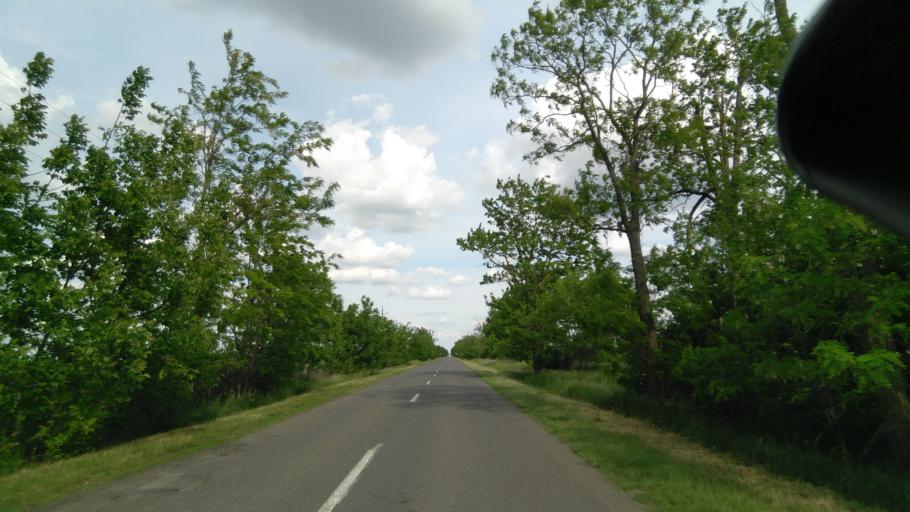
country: RO
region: Arad
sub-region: Comuna Peregu Mare
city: Peregu Mic
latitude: 46.2967
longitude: 20.9575
